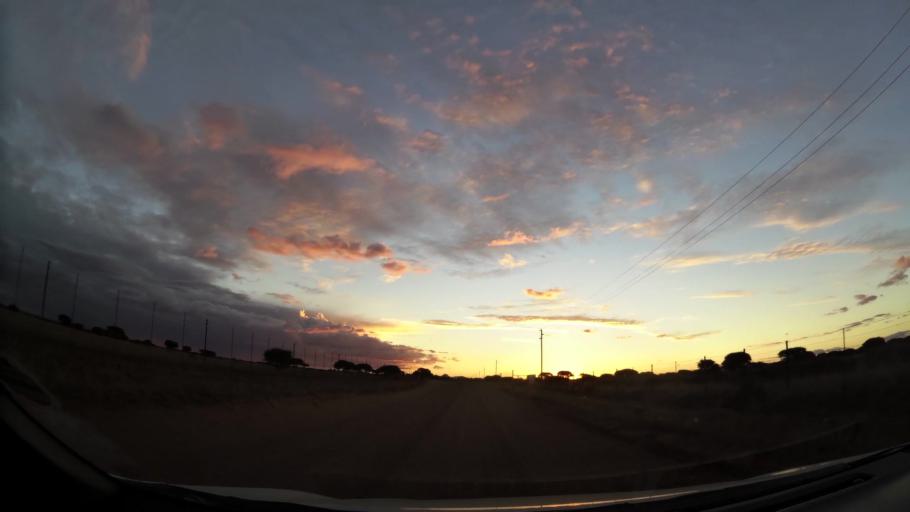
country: ZA
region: Limpopo
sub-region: Capricorn District Municipality
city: Polokwane
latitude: -23.7375
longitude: 29.4404
